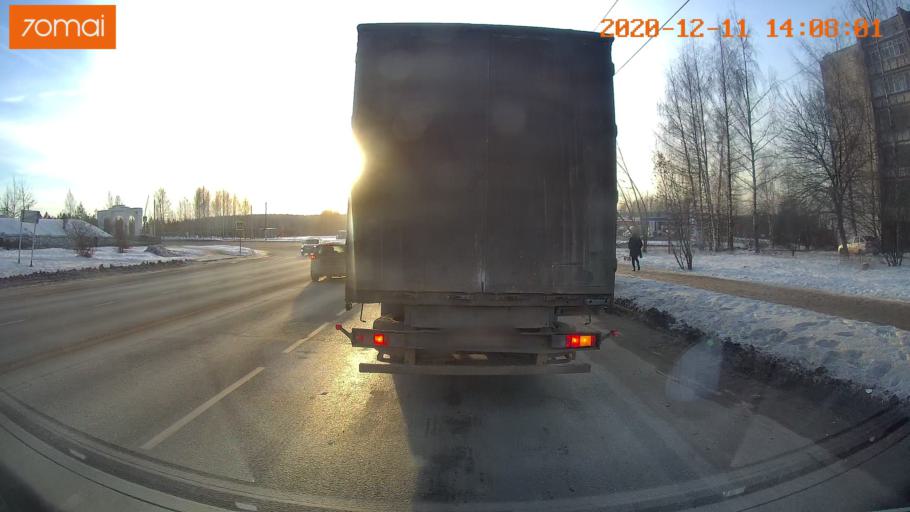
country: RU
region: Kostroma
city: Oktyabr'skiy
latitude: 57.7365
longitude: 40.9969
